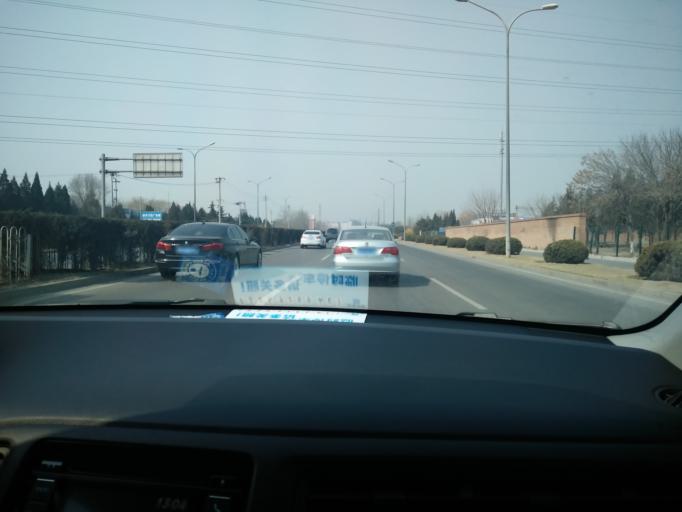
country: CN
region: Beijing
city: Jiugong
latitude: 39.8151
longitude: 116.4845
